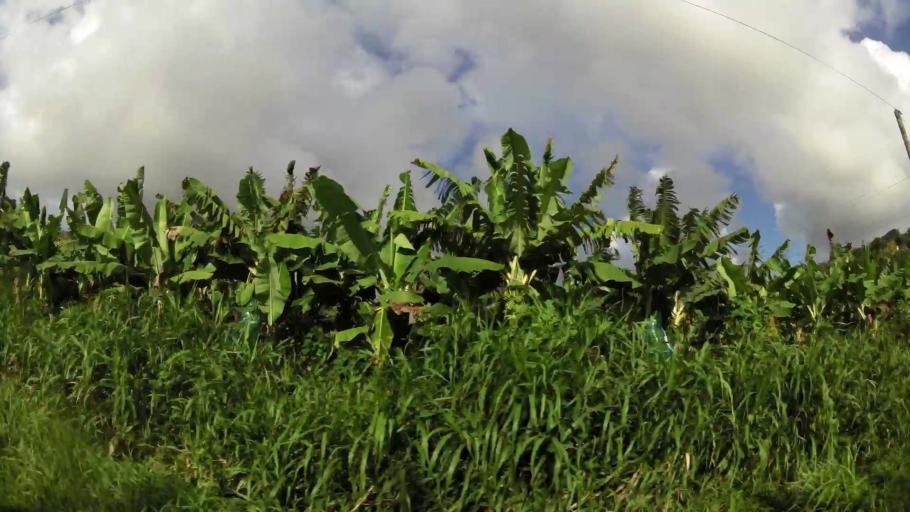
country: MQ
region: Martinique
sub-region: Martinique
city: Ducos
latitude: 14.5663
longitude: -60.9652
